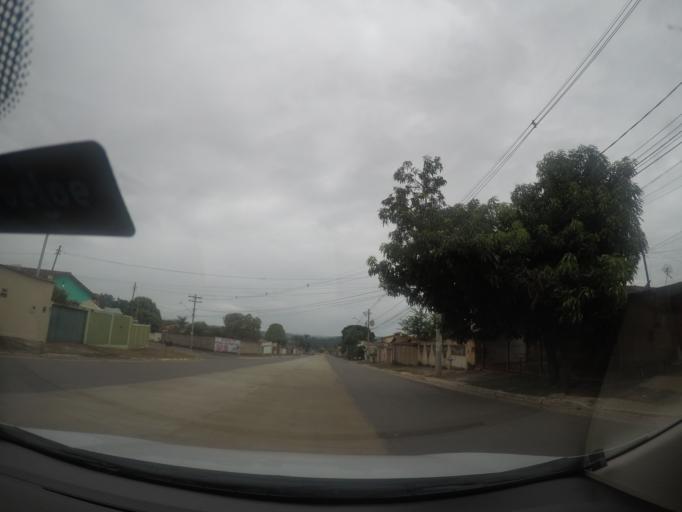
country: BR
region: Goias
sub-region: Goiania
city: Goiania
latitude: -16.6188
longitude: -49.3009
